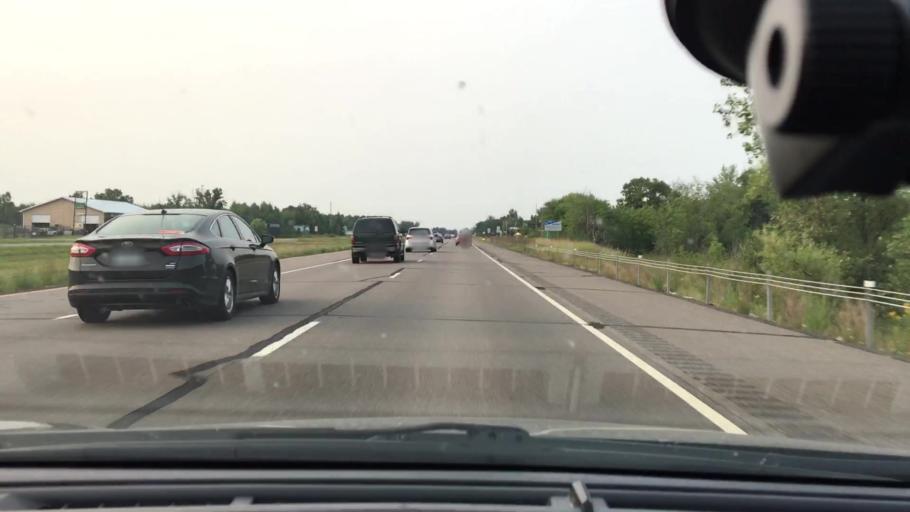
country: US
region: Minnesota
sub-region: Mille Lacs County
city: Vineland
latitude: 46.0504
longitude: -93.6624
